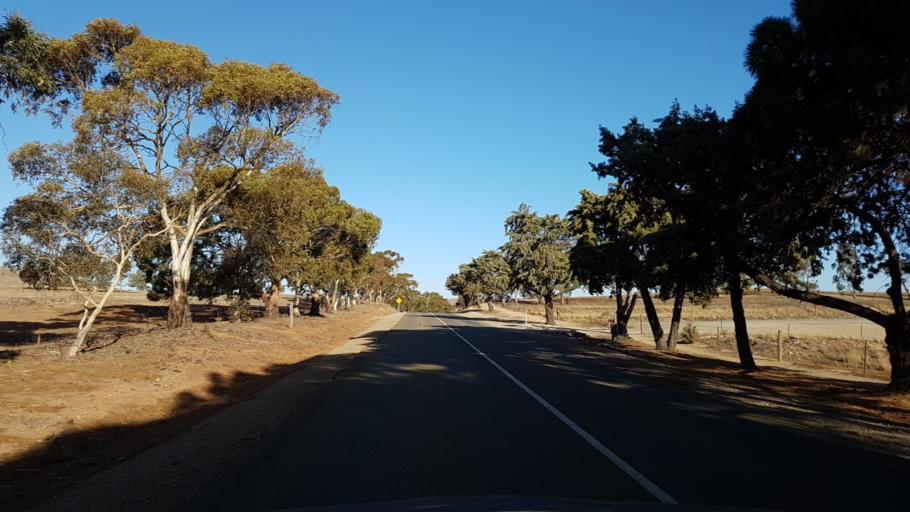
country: AU
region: South Australia
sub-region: Clare and Gilbert Valleys
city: Clare
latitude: -33.6739
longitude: 138.9377
